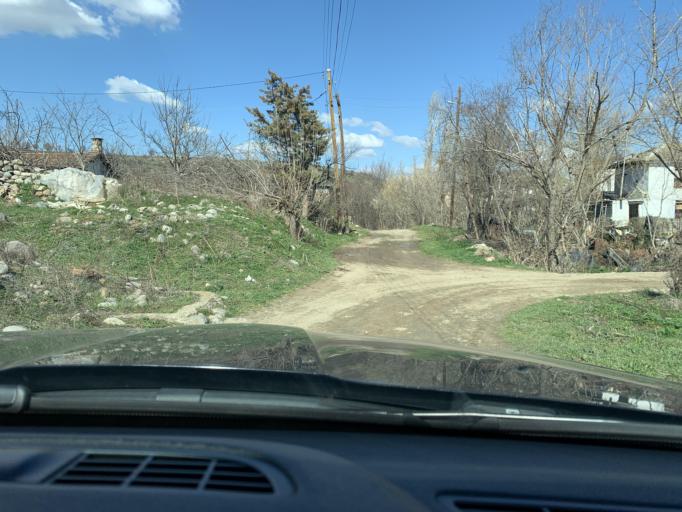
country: MK
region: Demir Kapija
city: Demir Kapija
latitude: 41.4181
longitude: 22.1662
